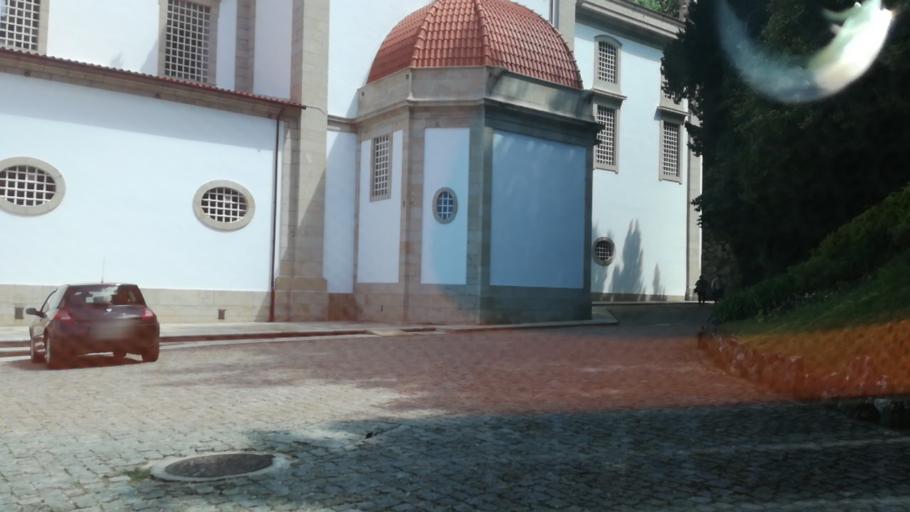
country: PT
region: Braga
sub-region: Braga
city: Adaufe
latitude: 41.5544
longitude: -8.3771
